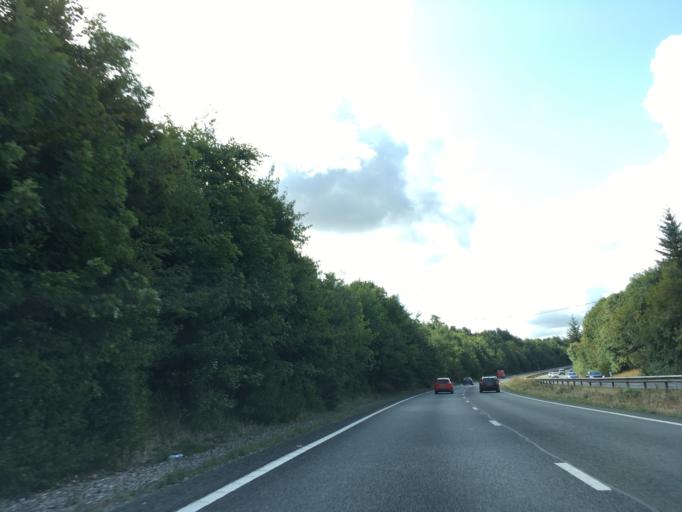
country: GB
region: England
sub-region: Hampshire
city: Highclere
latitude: 51.3407
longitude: -1.3404
